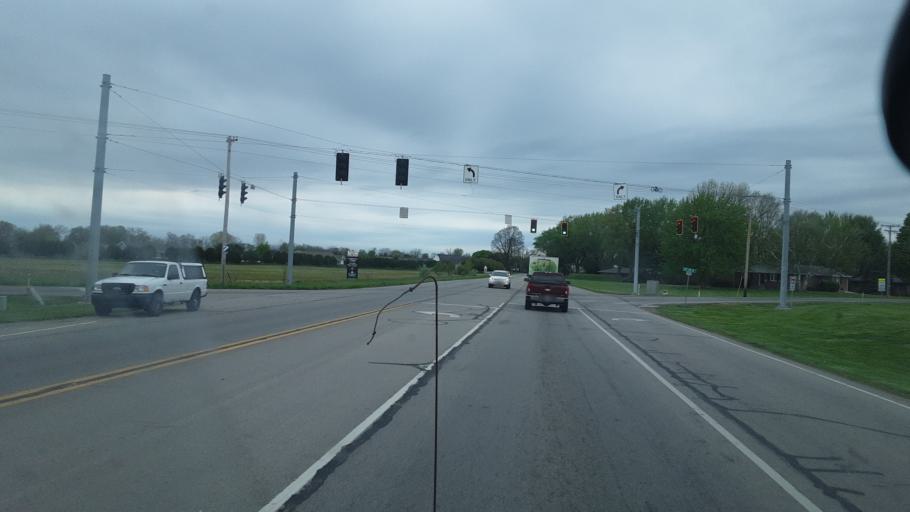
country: US
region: Indiana
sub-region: Elkhart County
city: New Paris
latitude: 41.5172
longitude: -85.7695
